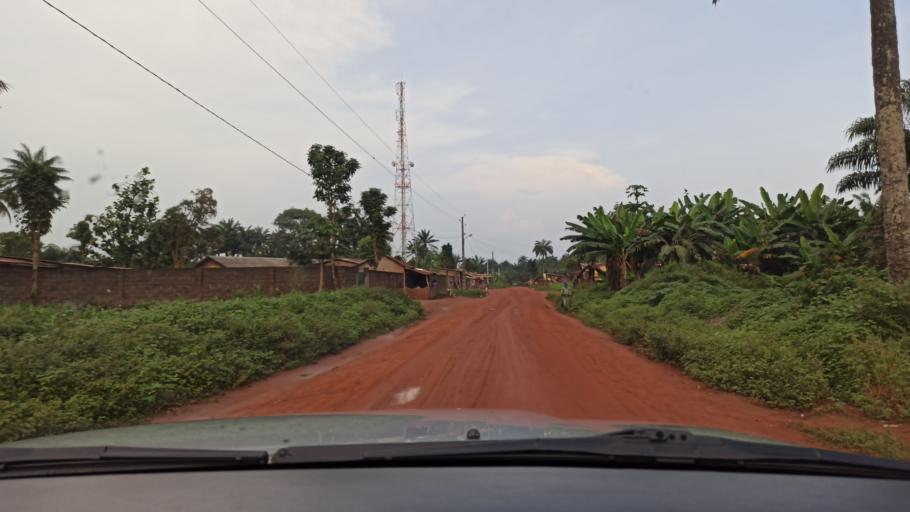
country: BJ
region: Queme
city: Porto-Novo
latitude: 6.4962
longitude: 2.6948
